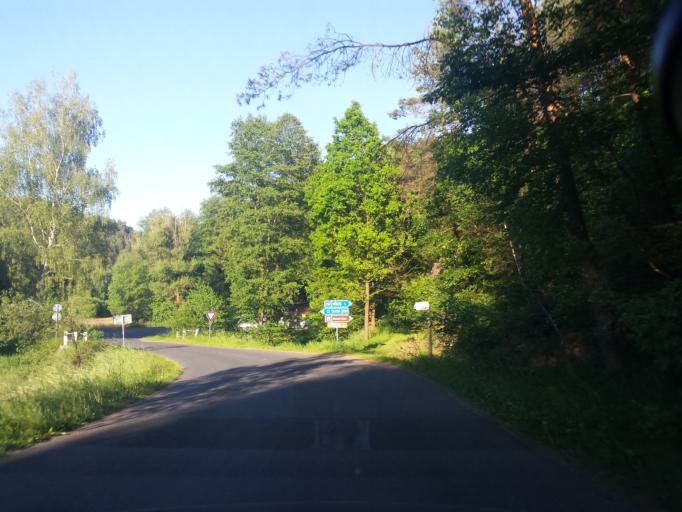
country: CZ
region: Central Bohemia
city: Mseno
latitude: 50.4637
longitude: 14.6138
